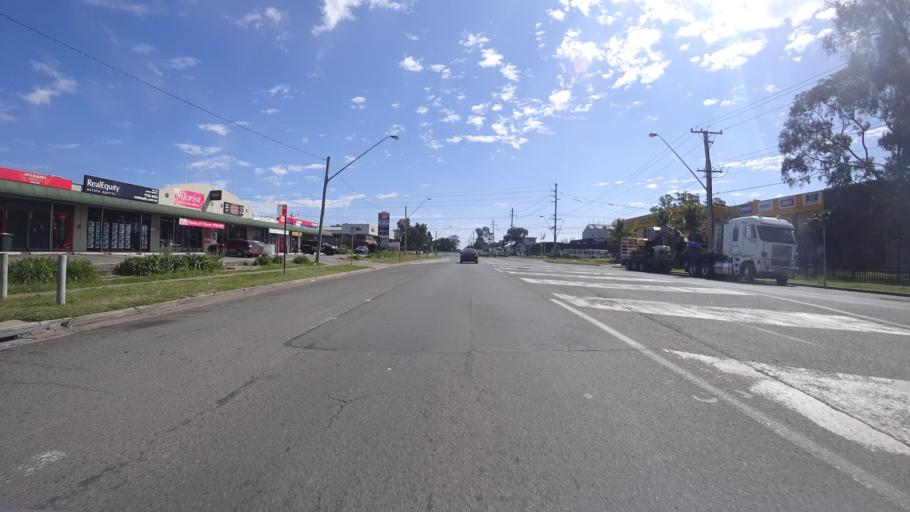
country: AU
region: New South Wales
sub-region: Bankstown
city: Milperra
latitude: -33.9239
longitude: 150.9621
